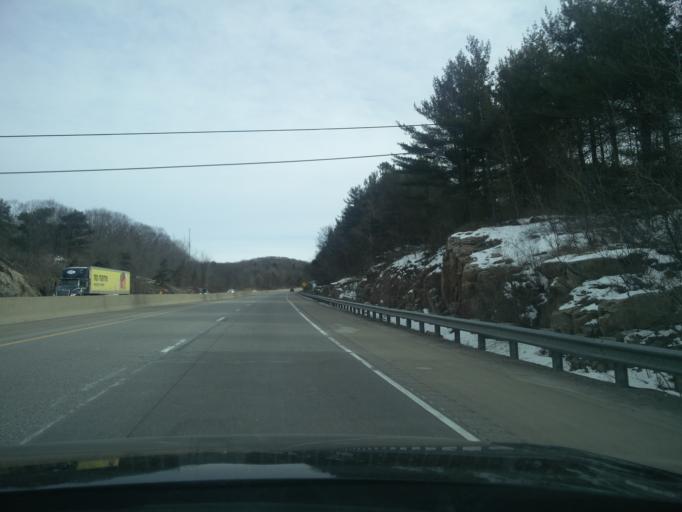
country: CA
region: Ontario
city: Brockville
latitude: 44.5814
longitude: -75.7322
